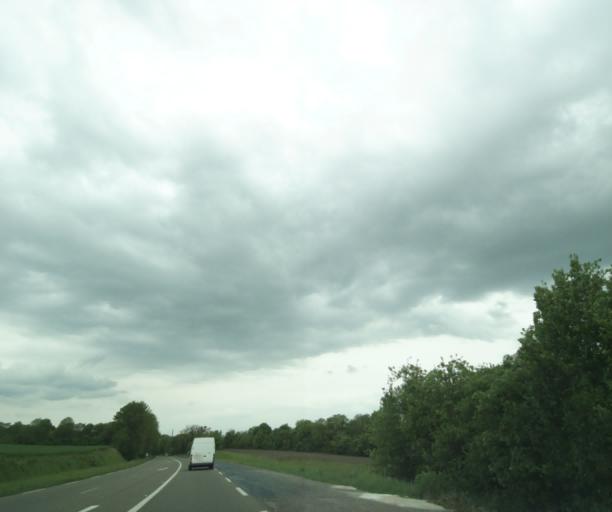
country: FR
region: Ile-de-France
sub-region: Departement des Yvelines
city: Flins-sur-Seine
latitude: 48.9596
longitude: 1.8817
